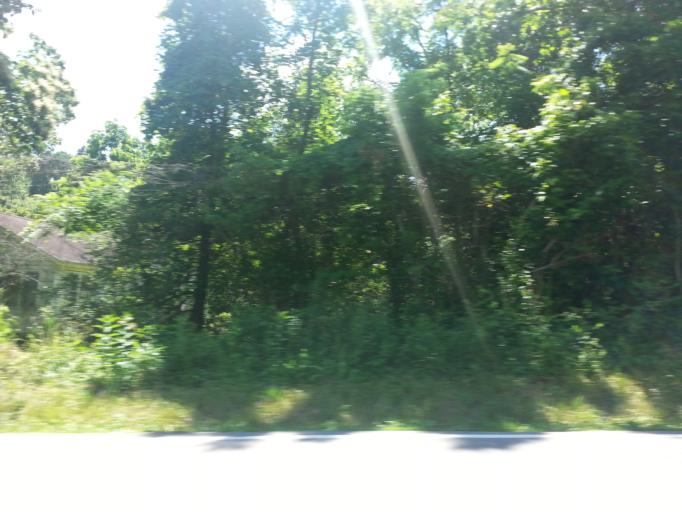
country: US
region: Virginia
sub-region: Lee County
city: Pennington Gap
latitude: 36.7364
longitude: -83.0005
